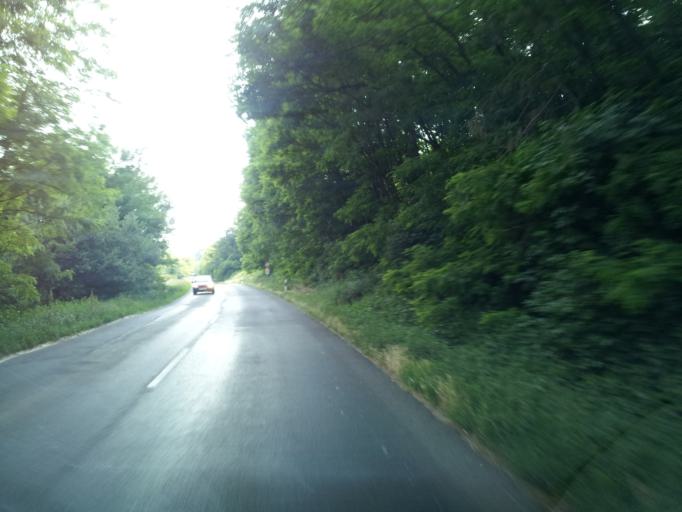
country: HU
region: Veszprem
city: Revfueloep
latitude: 46.9388
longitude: 17.5818
